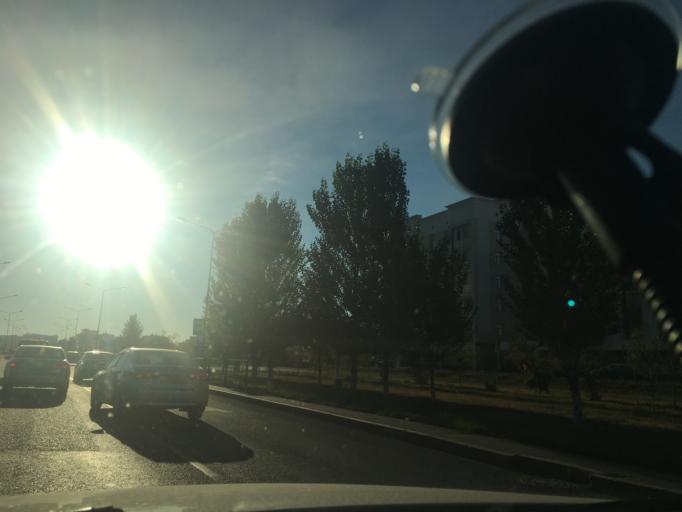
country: KZ
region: Astana Qalasy
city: Astana
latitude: 51.1479
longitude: 71.3925
